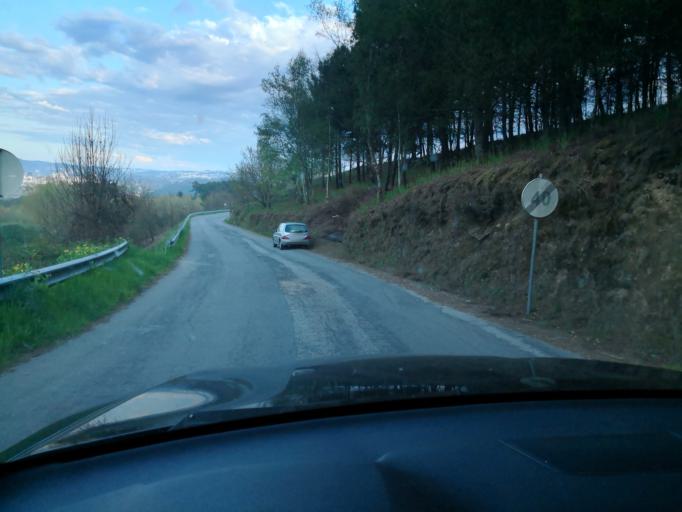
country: PT
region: Vila Real
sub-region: Vila Real
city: Vila Real
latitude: 41.3029
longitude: -7.7797
